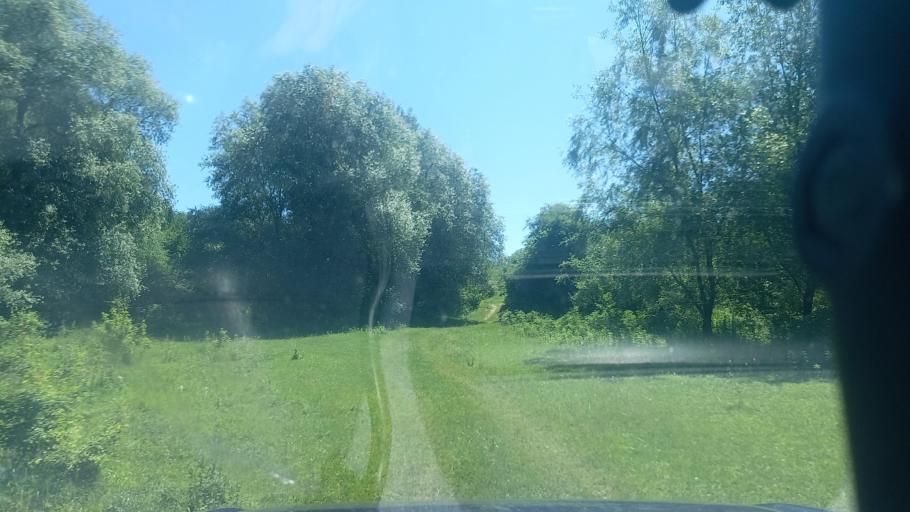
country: RU
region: Karachayevo-Cherkesiya
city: Kurdzhinovo
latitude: 44.1229
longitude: 41.0630
